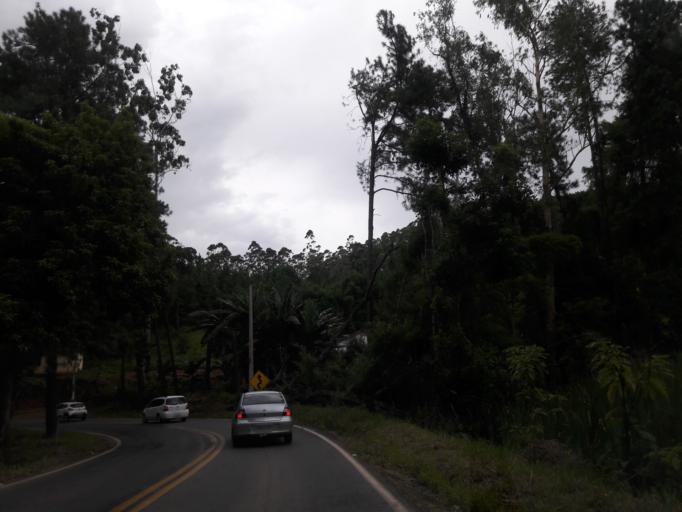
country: BR
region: Sao Paulo
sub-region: Aruja
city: Aruja
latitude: -23.3443
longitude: -46.4297
